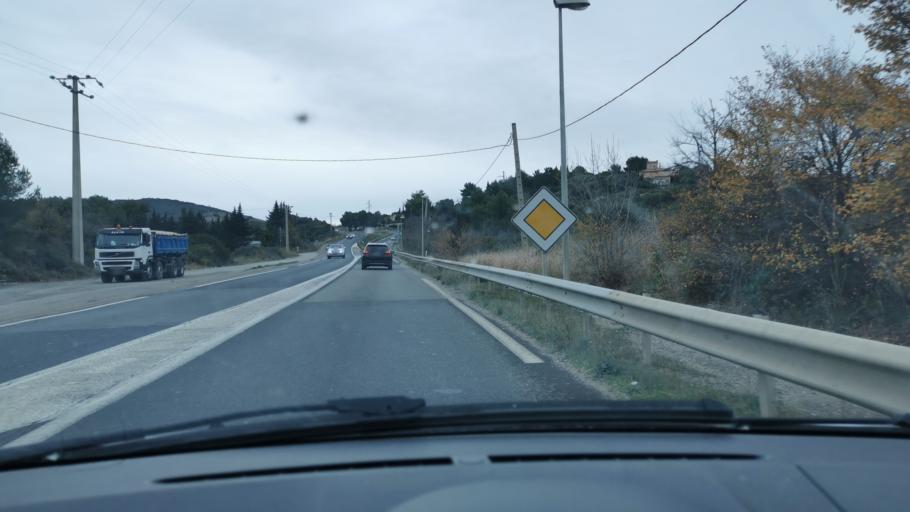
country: FR
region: Languedoc-Roussillon
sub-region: Departement de l'Herault
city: Mireval
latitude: 43.5144
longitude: 3.8060
